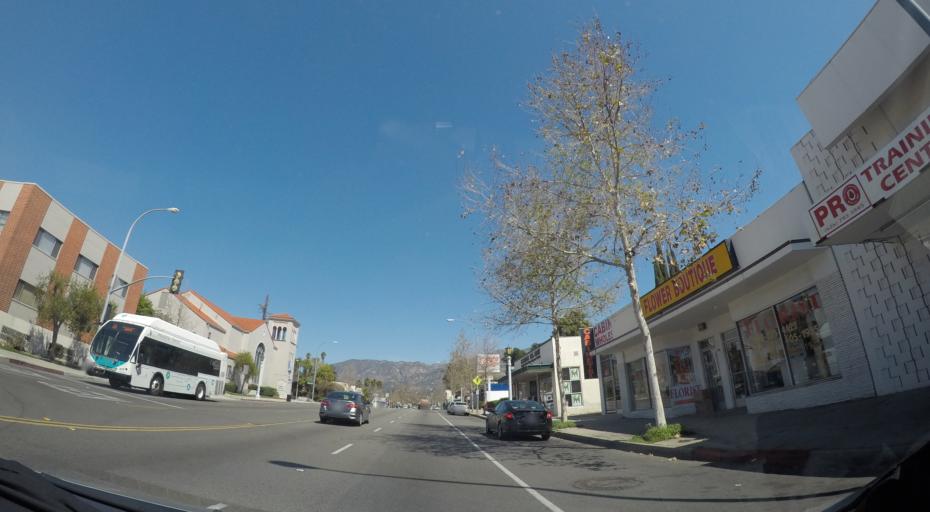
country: US
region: California
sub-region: Los Angeles County
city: Pasadena
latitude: 34.1549
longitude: -118.1324
